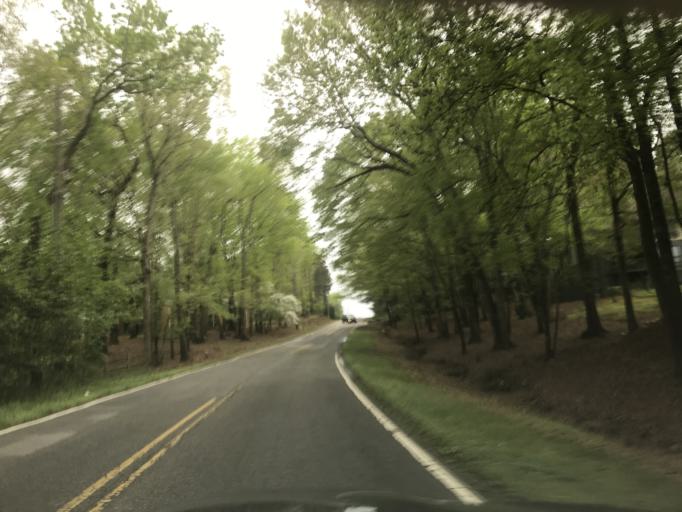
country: US
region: North Carolina
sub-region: Wake County
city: West Raleigh
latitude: 35.7545
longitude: -78.7051
